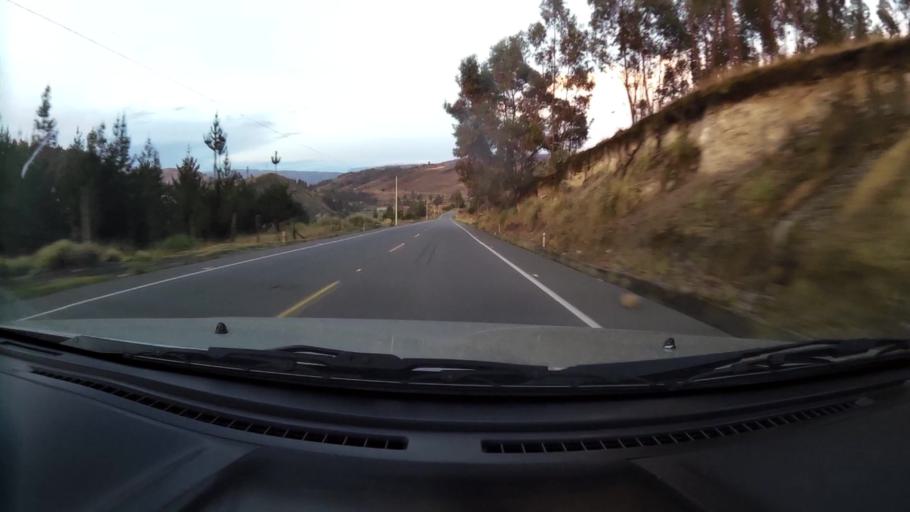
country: EC
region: Chimborazo
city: Alausi
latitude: -1.9624
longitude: -78.7196
